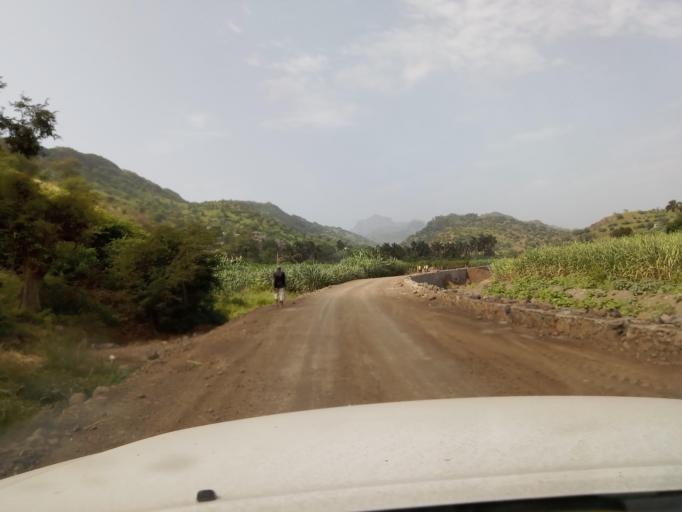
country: CV
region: Santa Cruz
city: Santa Cruz
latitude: 15.1143
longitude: -23.5506
